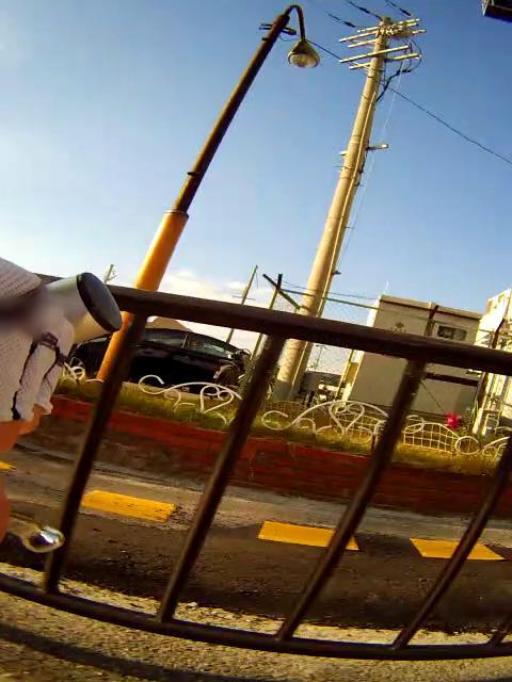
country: JP
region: Hyogo
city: Itami
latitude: 34.7841
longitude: 135.3991
